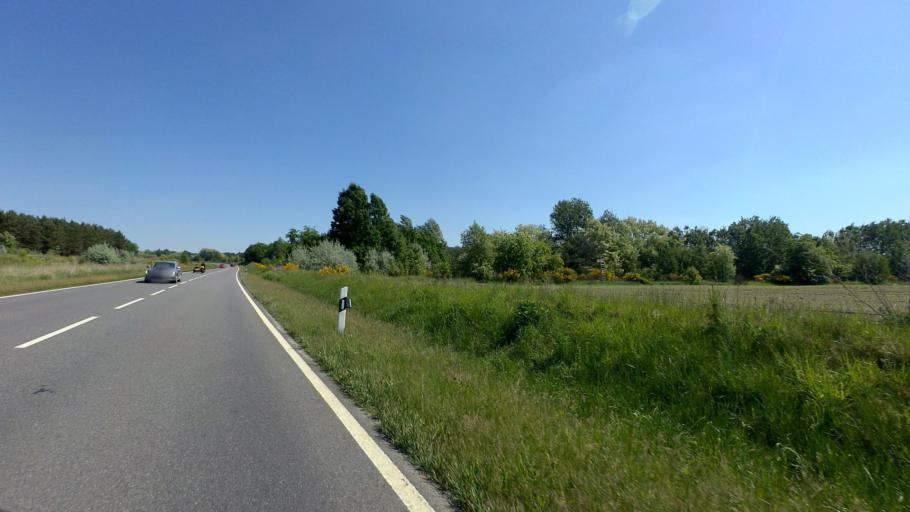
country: DE
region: Brandenburg
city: Spremberg
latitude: 51.5742
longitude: 14.3370
